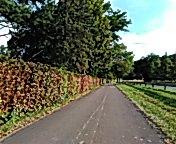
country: LU
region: Grevenmacher
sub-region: Canton d'Echternach
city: Rosport
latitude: 49.7977
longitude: 6.5086
